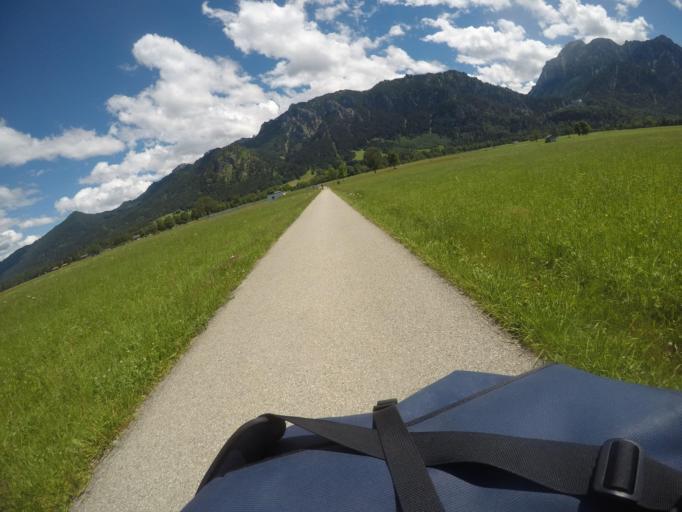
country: DE
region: Bavaria
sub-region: Swabia
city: Schwangau
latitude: 47.5744
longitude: 10.7432
